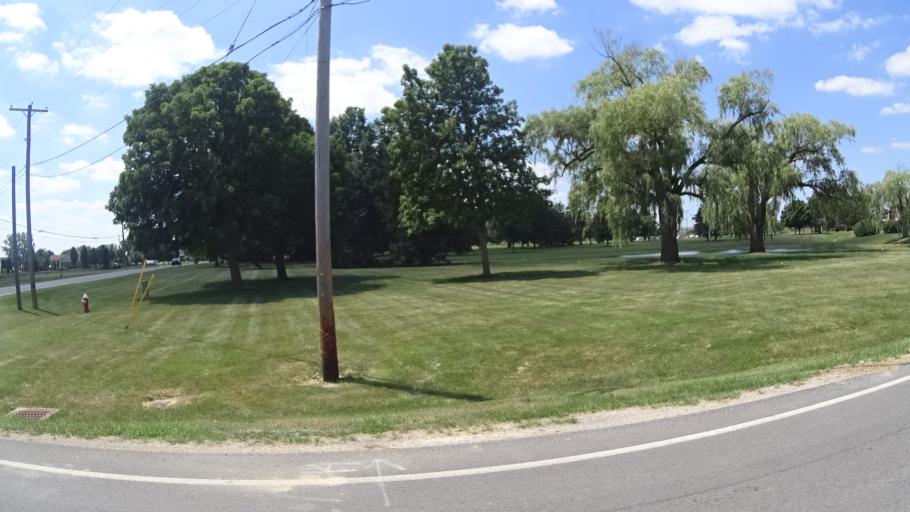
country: US
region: Ohio
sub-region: Erie County
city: Huron
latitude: 41.3986
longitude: -82.5913
